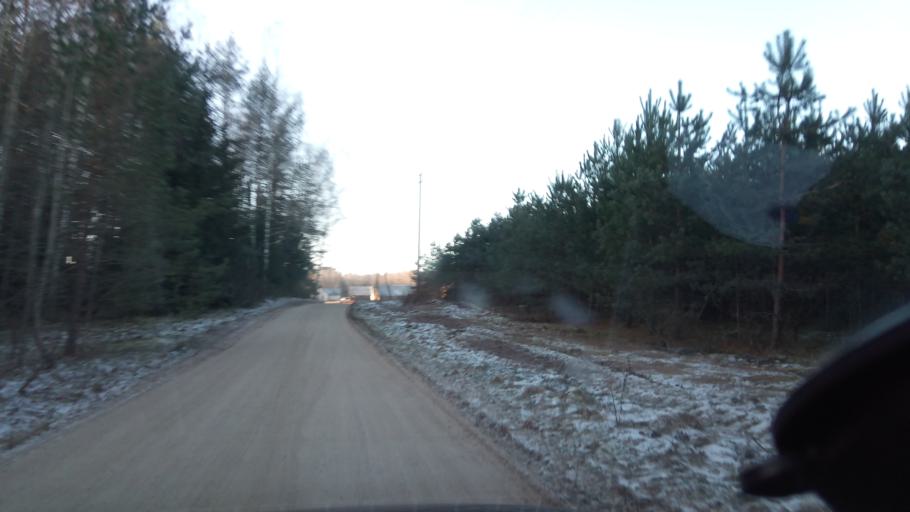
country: LT
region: Alytaus apskritis
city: Druskininkai
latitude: 54.1603
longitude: 23.9561
